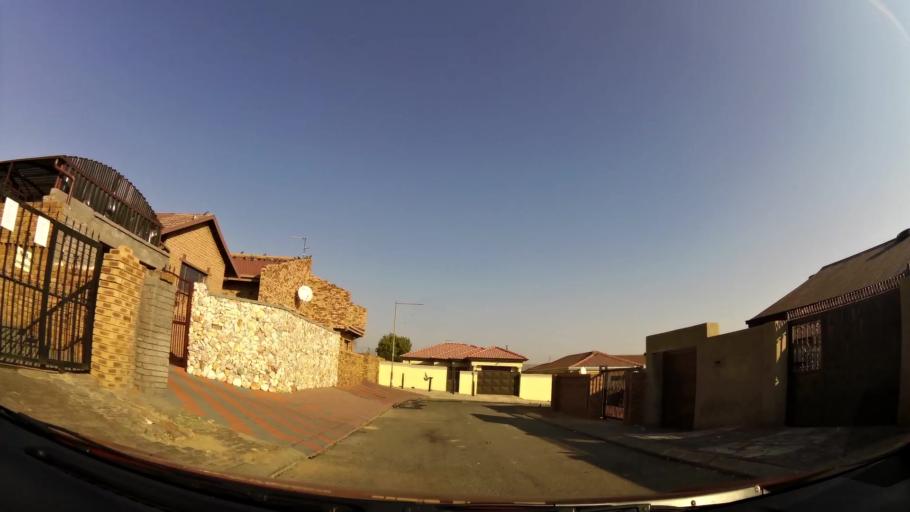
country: ZA
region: Gauteng
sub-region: City of Johannesburg Metropolitan Municipality
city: Soweto
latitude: -26.2579
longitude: 27.9495
